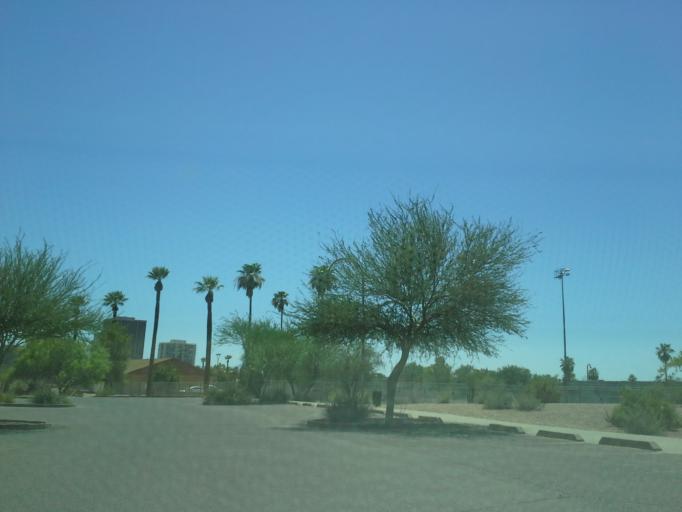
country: US
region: Arizona
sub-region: Maricopa County
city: Phoenix
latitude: 33.5005
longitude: -112.0716
